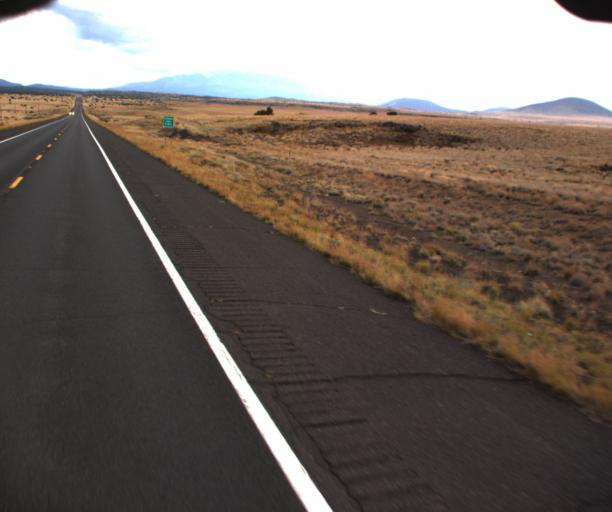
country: US
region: Arizona
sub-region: Coconino County
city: Flagstaff
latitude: 35.5634
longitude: -111.5336
